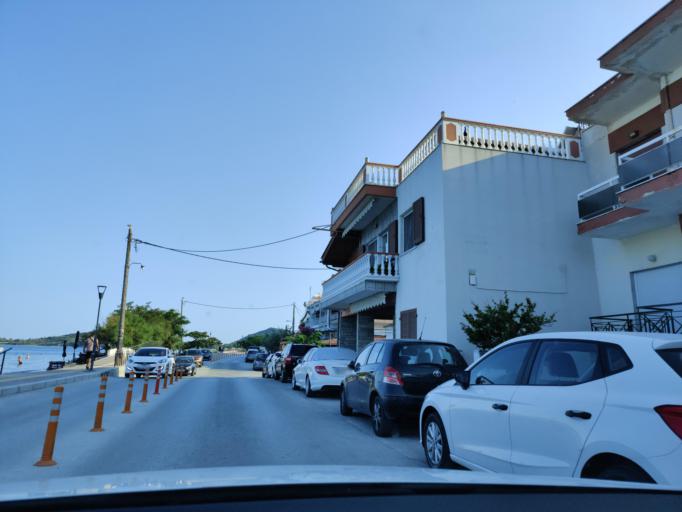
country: GR
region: East Macedonia and Thrace
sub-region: Nomos Kavalas
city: Nea Peramos
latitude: 40.8363
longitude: 24.3053
